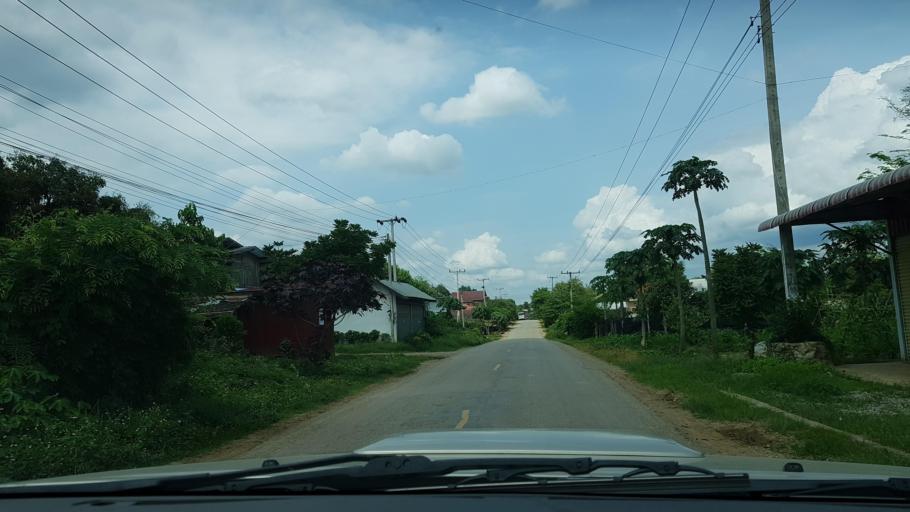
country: LA
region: Loungnamtha
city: Muang Nale
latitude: 20.0462
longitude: 101.3533
